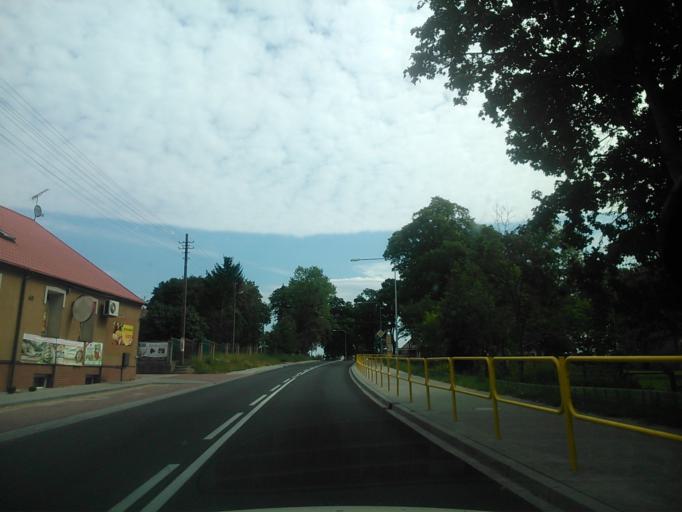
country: PL
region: Warmian-Masurian Voivodeship
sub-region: Powiat dzialdowski
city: Dzialdowo
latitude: 53.2334
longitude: 20.0328
